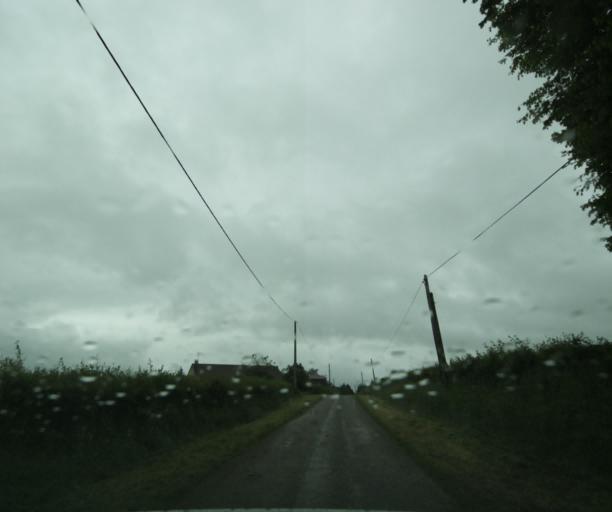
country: FR
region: Bourgogne
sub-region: Departement de Saone-et-Loire
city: Charolles
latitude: 46.4781
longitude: 4.2960
